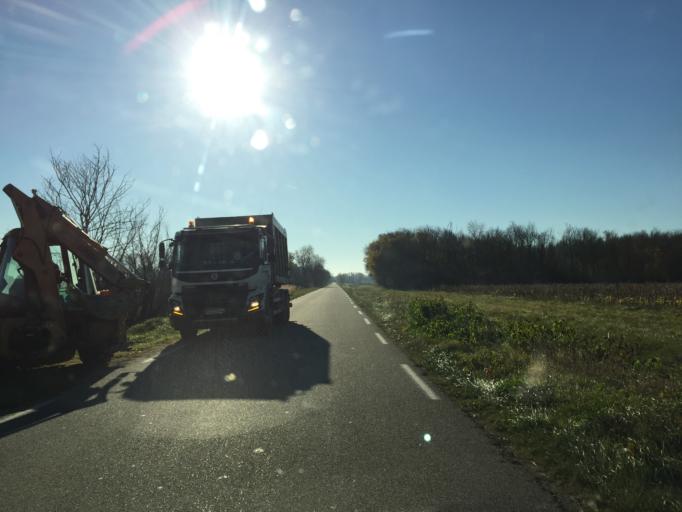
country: FR
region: Provence-Alpes-Cote d'Azur
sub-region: Departement du Vaucluse
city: Bedarrides
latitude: 44.0285
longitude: 4.9152
